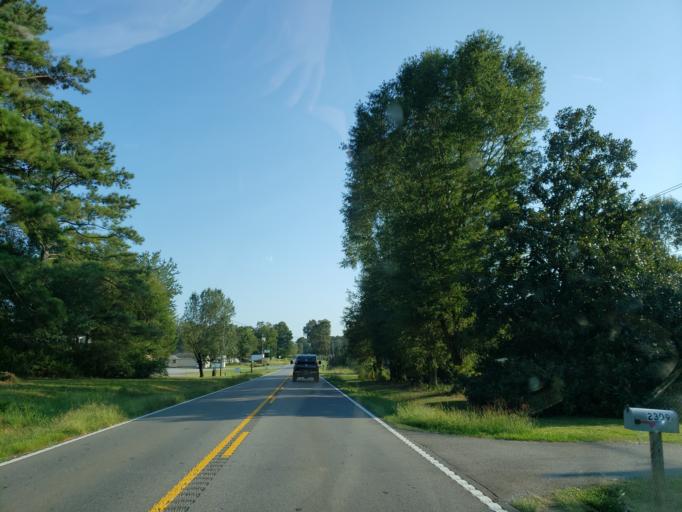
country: US
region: Georgia
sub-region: Murray County
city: Chatsworth
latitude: 34.7951
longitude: -84.8234
